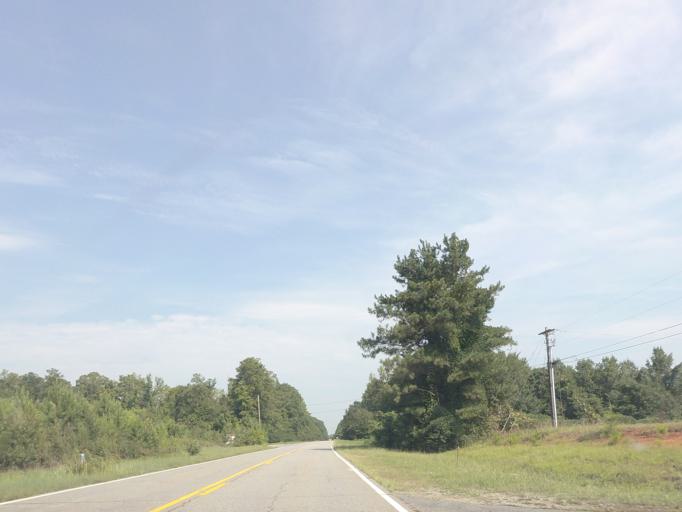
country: US
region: Georgia
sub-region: Bibb County
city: Macon
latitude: 32.9129
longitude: -83.6978
